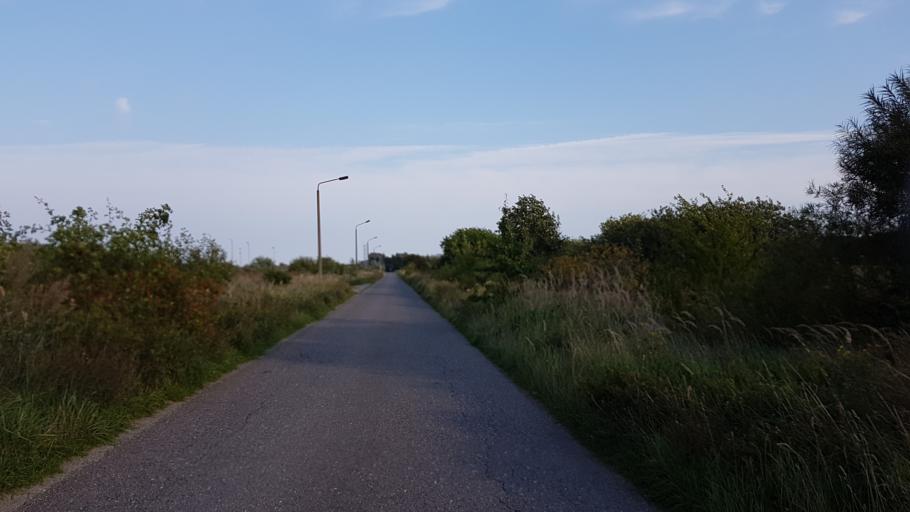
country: DE
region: Mecklenburg-Vorpommern
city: Sagard
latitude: 54.5003
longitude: 13.5396
